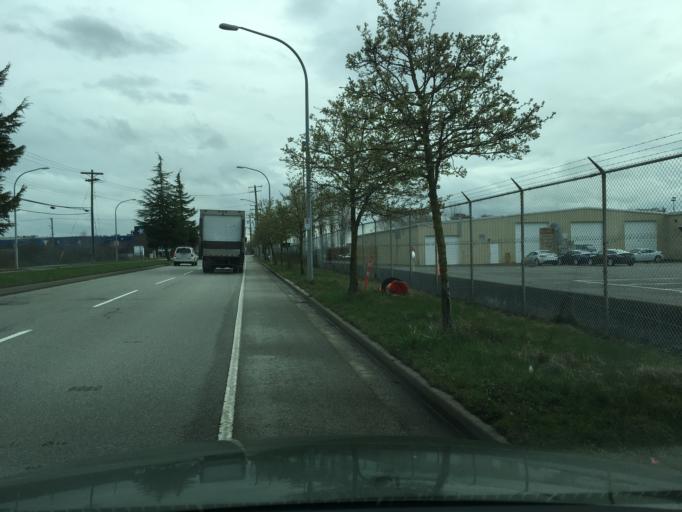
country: CA
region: British Columbia
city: Ladner
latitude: 49.1335
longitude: -123.0711
